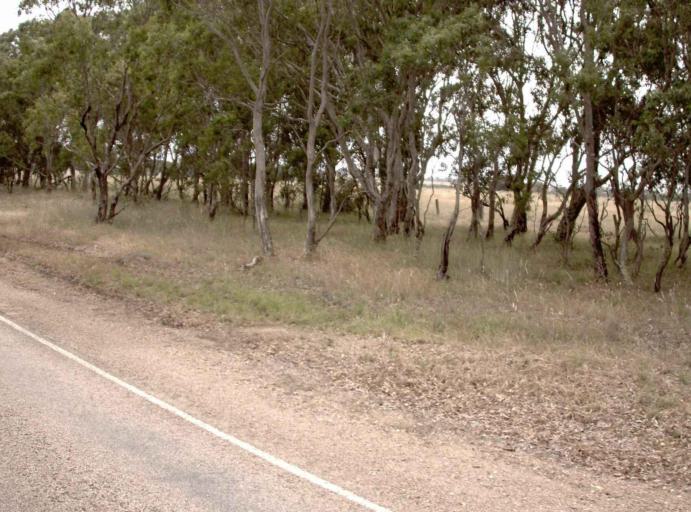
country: AU
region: Victoria
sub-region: Wellington
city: Sale
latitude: -37.9397
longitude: 147.0935
